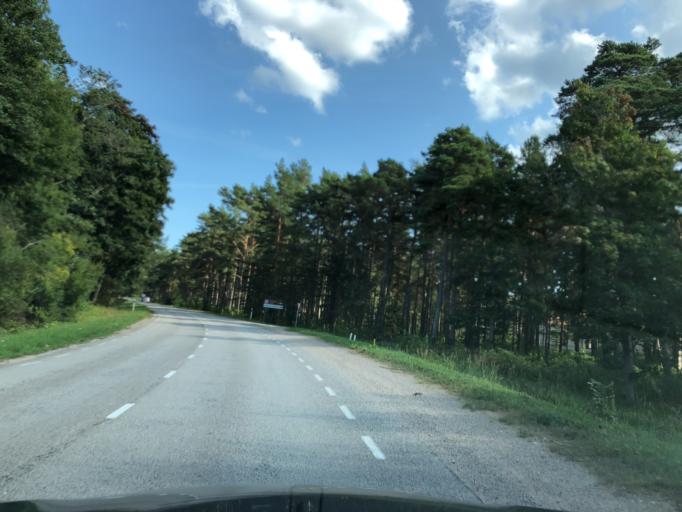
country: EE
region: Hiiumaa
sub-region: Kaerdla linn
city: Kardla
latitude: 58.7080
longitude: 22.5890
